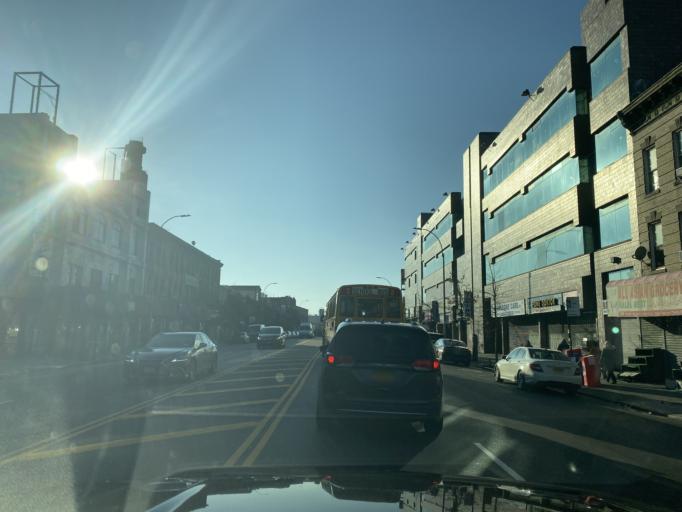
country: US
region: New York
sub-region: Kings County
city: Brooklyn
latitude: 40.6314
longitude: -73.9666
